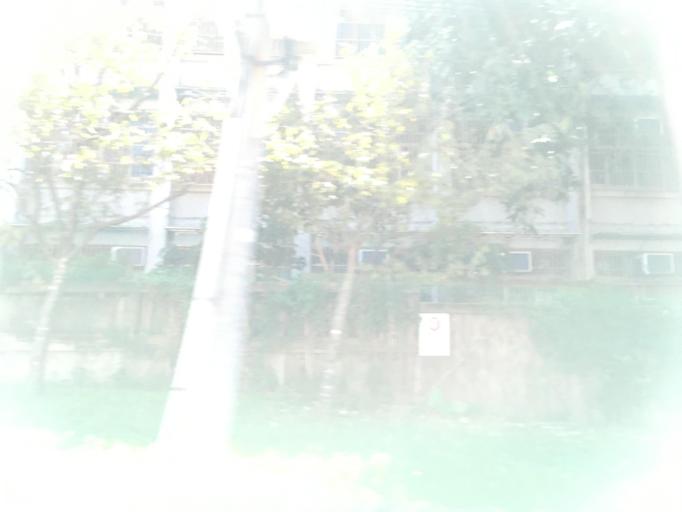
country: TW
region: Taipei
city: Taipei
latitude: 25.1445
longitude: 121.5027
